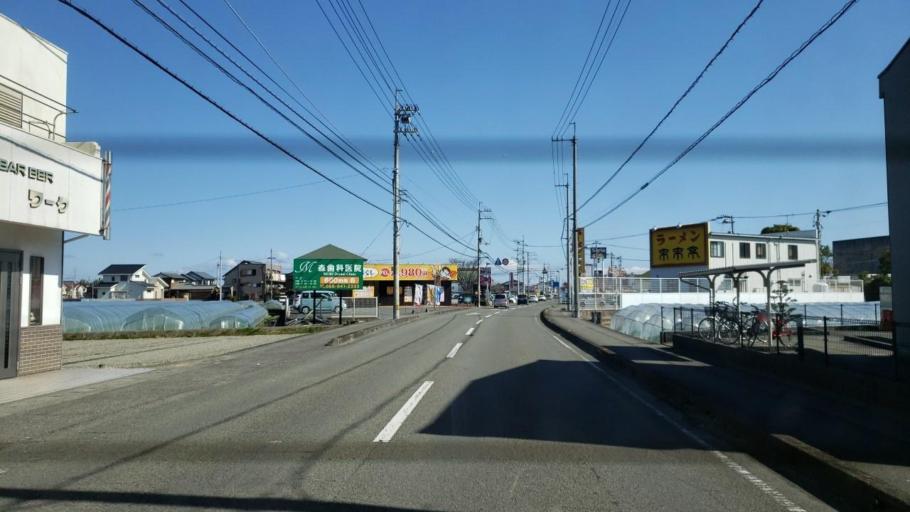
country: JP
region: Tokushima
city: Tokushima-shi
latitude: 34.1339
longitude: 134.5107
